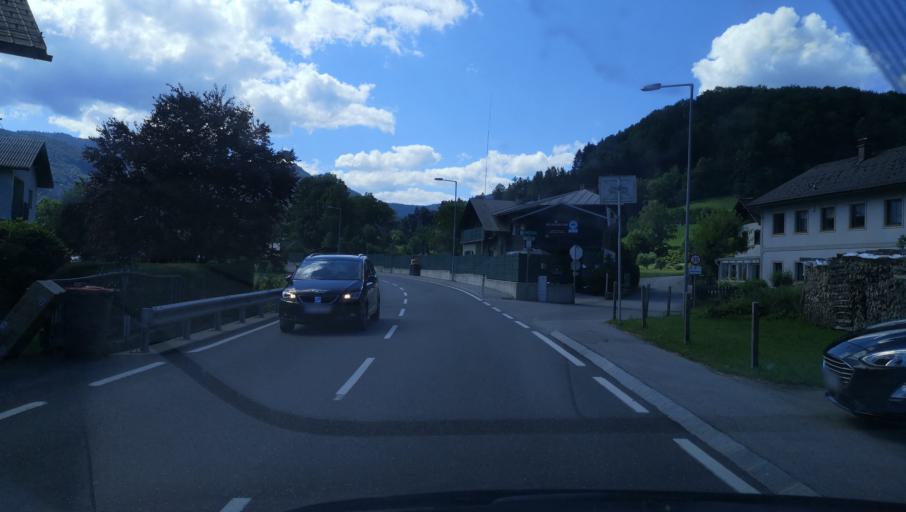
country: AT
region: Lower Austria
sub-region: Politischer Bezirk Scheibbs
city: Gresten
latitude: 47.9635
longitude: 15.0238
